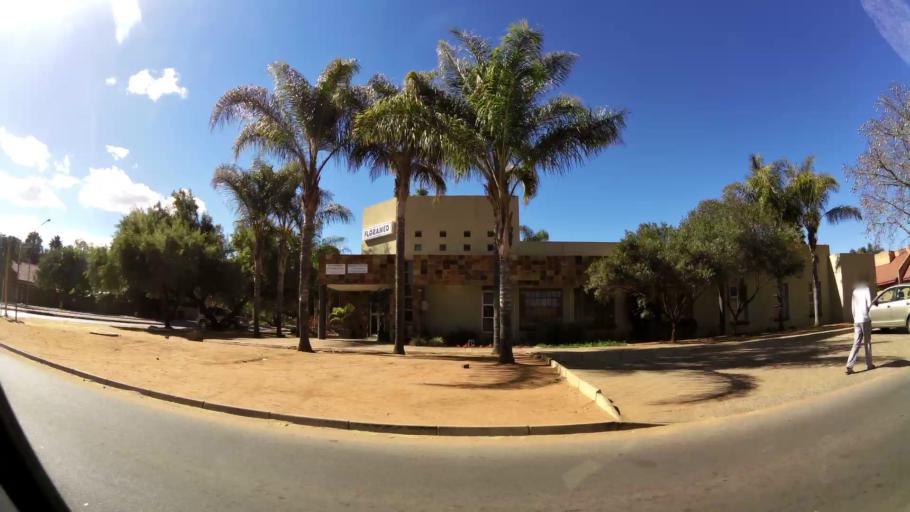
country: ZA
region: Limpopo
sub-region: Capricorn District Municipality
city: Polokwane
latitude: -23.9084
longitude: 29.4903
